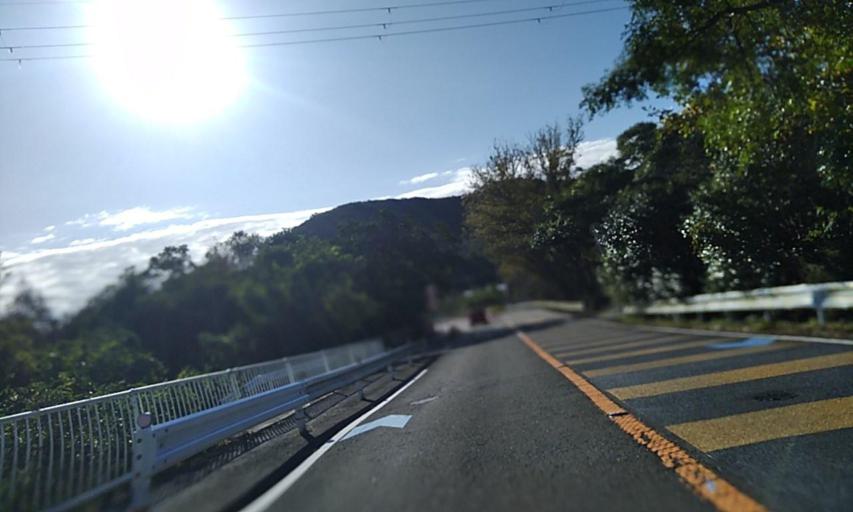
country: JP
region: Wakayama
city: Minato
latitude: 34.2708
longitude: 135.0849
